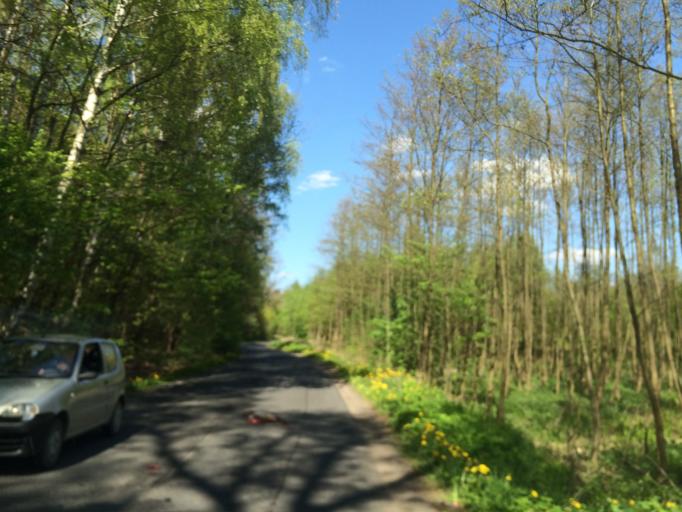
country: PL
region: Warmian-Masurian Voivodeship
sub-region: Powiat ilawski
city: Lubawa
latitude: 53.3996
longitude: 19.7455
